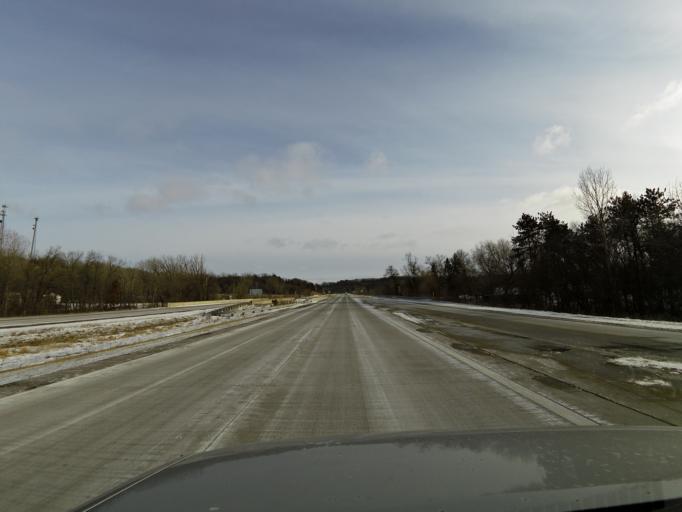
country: US
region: Wisconsin
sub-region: Pierce County
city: River Falls
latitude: 44.8768
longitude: -92.6199
